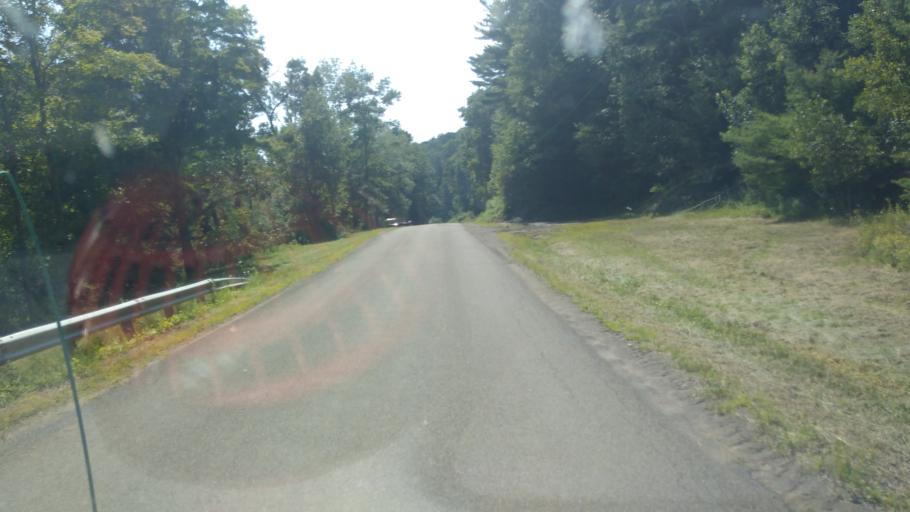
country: US
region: New York
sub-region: Steuben County
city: Canisteo
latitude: 42.3018
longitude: -77.6109
